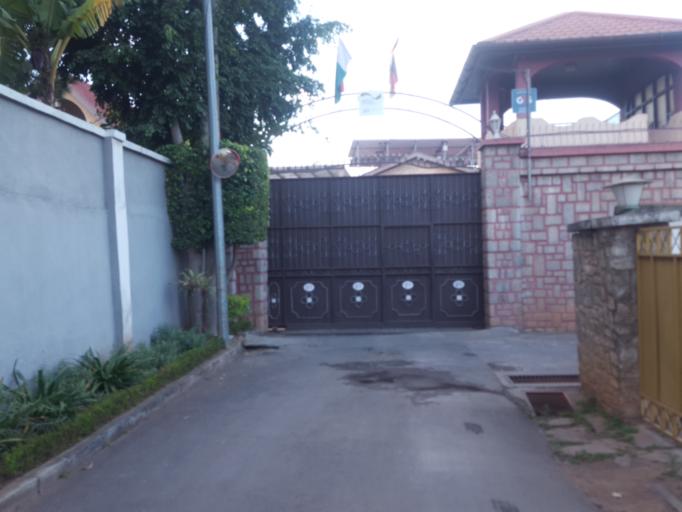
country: MG
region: Analamanga
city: Antananarivo
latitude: -18.8678
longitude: 47.5334
